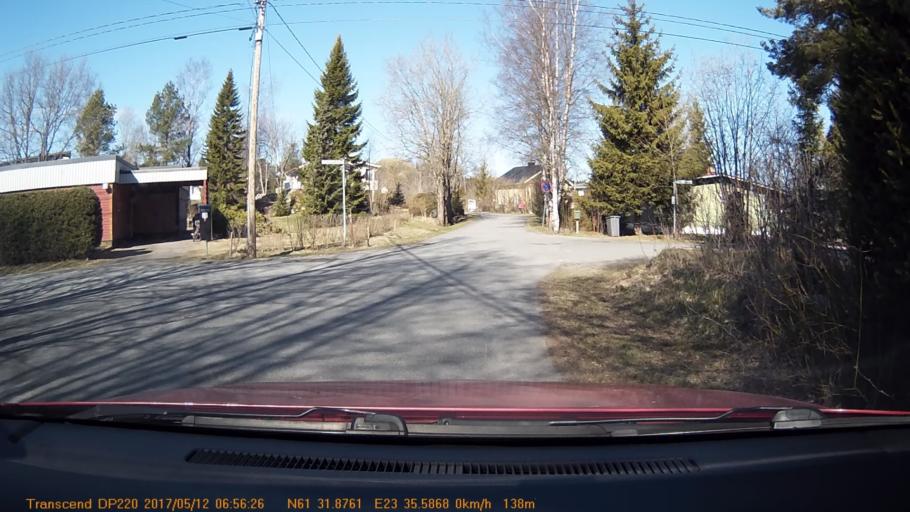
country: FI
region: Pirkanmaa
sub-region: Tampere
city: Yloejaervi
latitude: 61.5313
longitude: 23.5932
